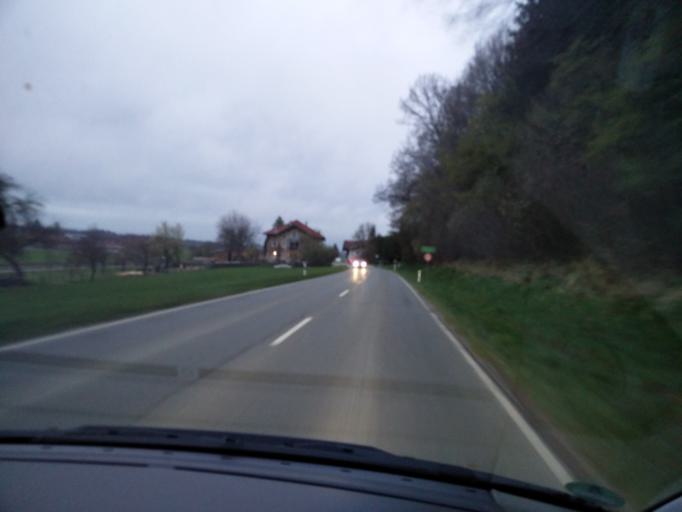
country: DE
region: Bavaria
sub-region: Upper Bavaria
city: Bad Endorf
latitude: 47.9288
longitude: 12.2876
